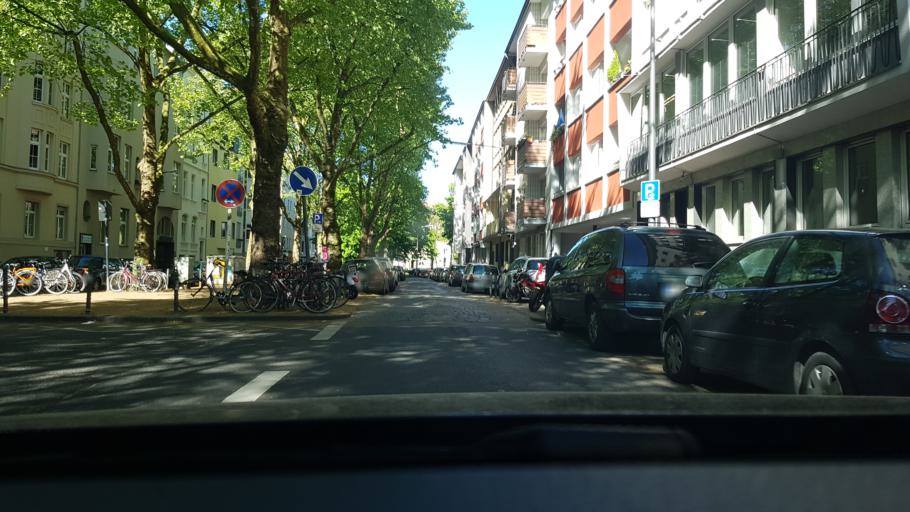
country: DE
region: North Rhine-Westphalia
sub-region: Regierungsbezirk Koln
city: Neustadt/Nord
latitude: 50.9542
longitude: 6.9564
